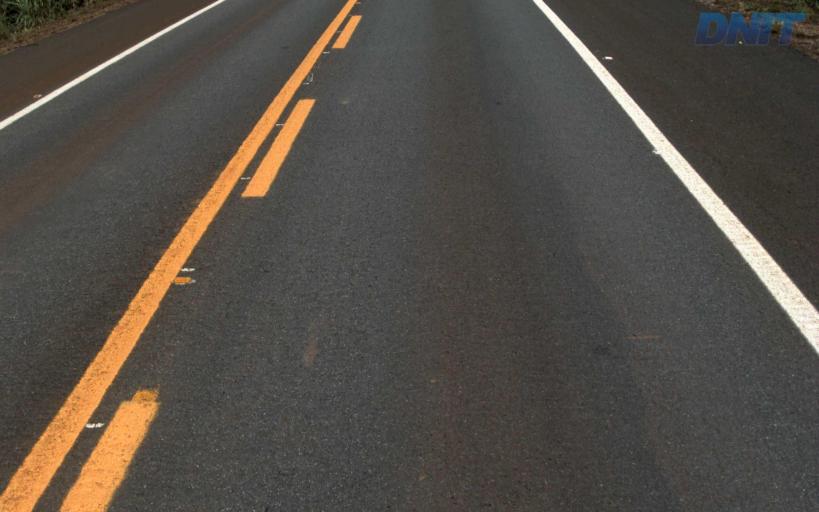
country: BR
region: Goias
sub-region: Barro Alto
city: Barro Alto
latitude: -15.1839
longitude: -48.7838
